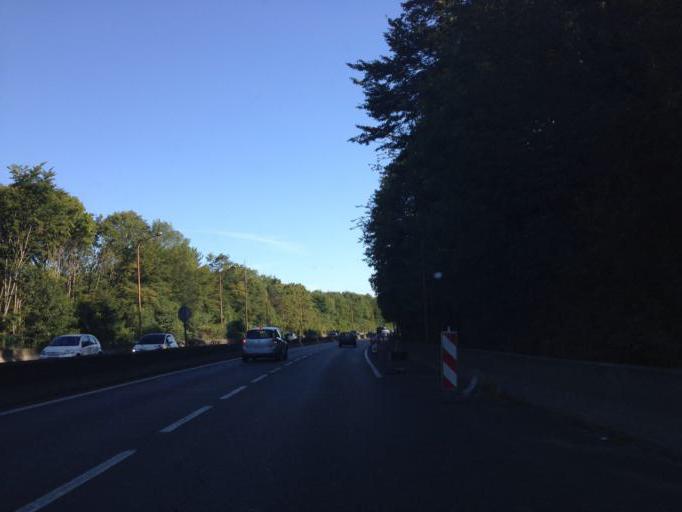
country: FR
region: Ile-de-France
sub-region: Departement des Hauts-de-Seine
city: Sevres
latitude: 48.8075
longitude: 2.2123
